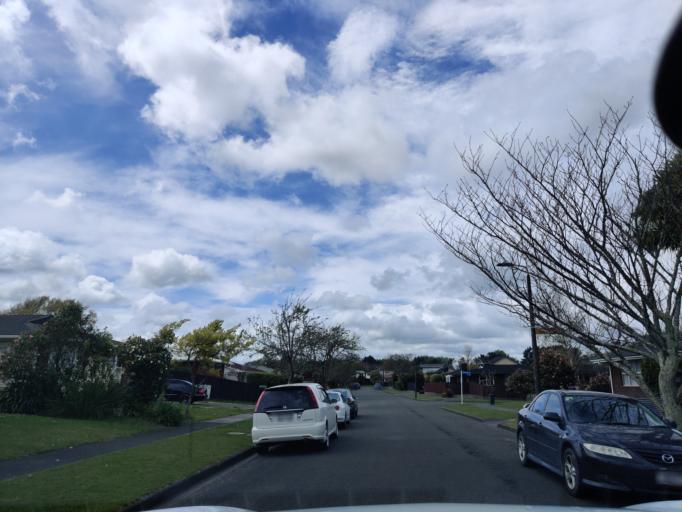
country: NZ
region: Manawatu-Wanganui
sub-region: Palmerston North City
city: Palmerston North
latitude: -40.3803
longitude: 175.5955
